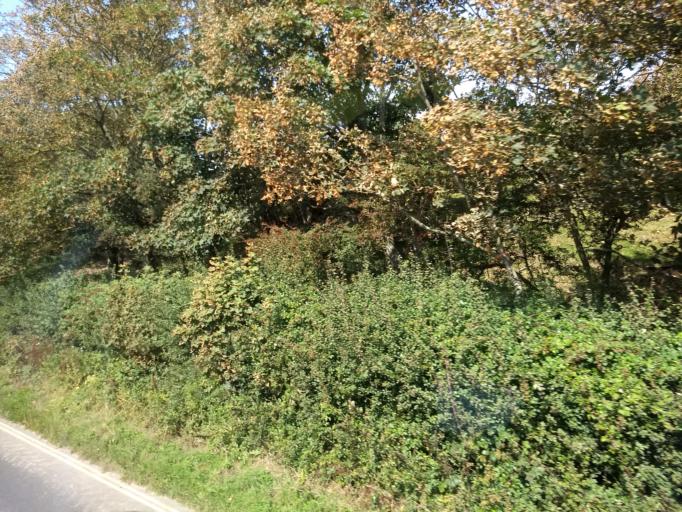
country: GB
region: England
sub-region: Isle of Wight
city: Totland
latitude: 50.6690
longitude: -1.5605
